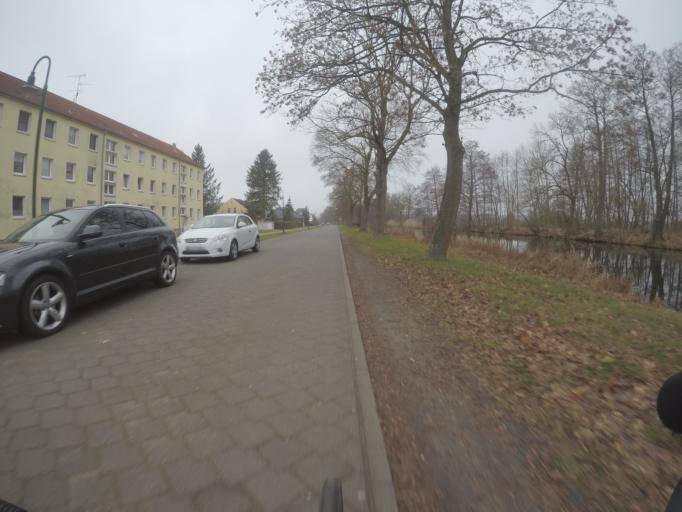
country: DE
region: Brandenburg
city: Marienwerder
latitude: 52.8484
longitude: 13.5349
